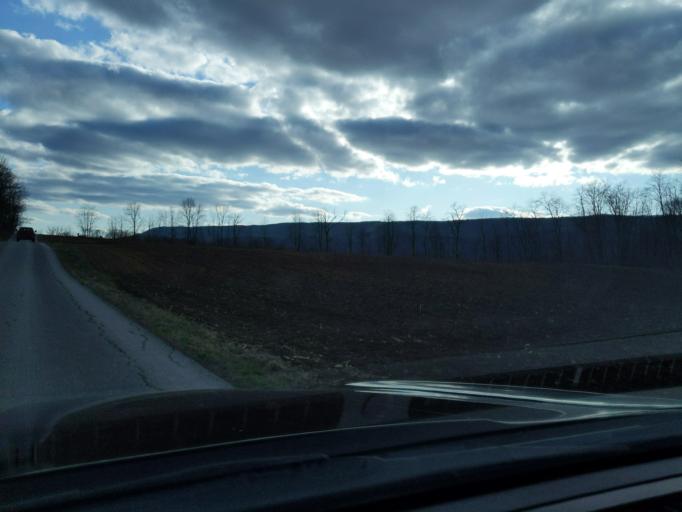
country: US
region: Pennsylvania
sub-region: Blair County
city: Tipton
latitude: 40.5891
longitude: -78.2559
